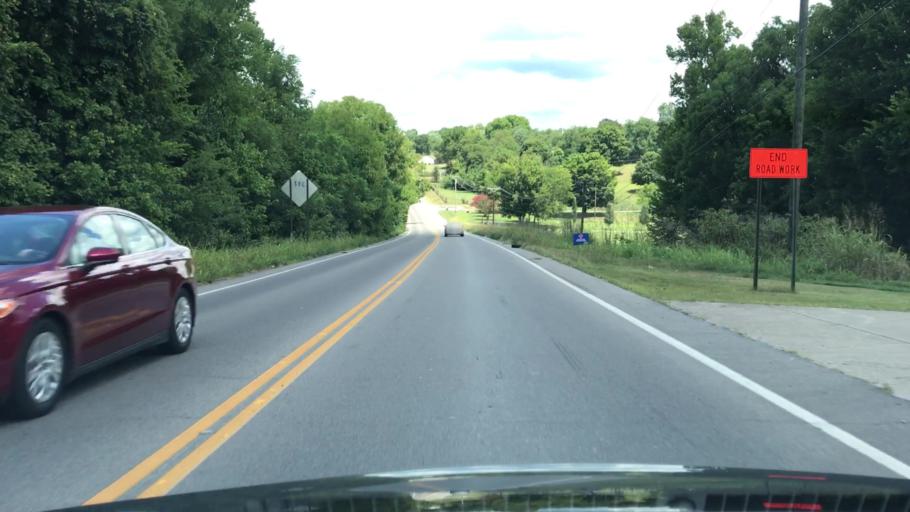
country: US
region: Tennessee
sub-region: Williamson County
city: Nolensville
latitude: 35.8588
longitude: -86.6585
